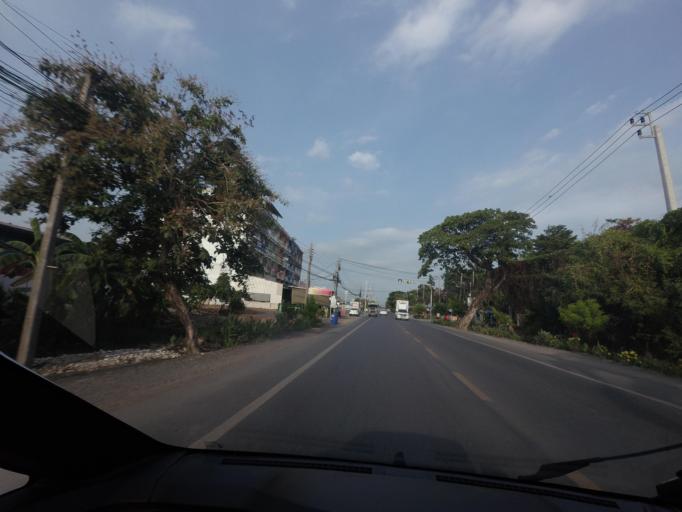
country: TH
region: Bangkok
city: Nong Chok
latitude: 13.8524
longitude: 100.8753
